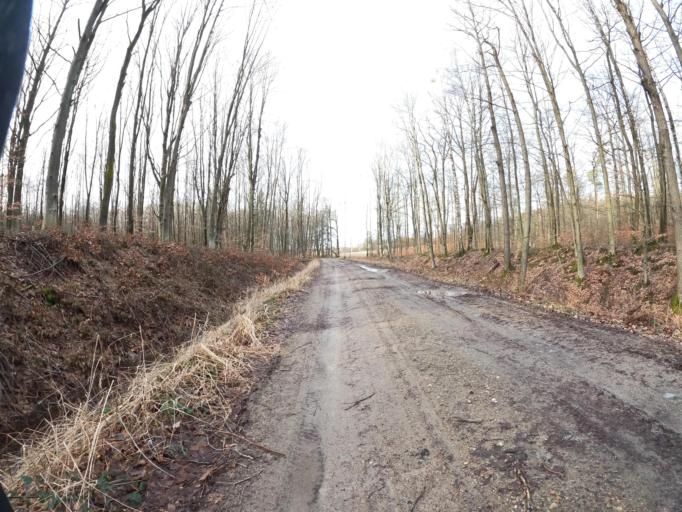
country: PL
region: West Pomeranian Voivodeship
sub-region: Powiat koszalinski
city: Polanow
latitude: 54.1724
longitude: 16.7492
